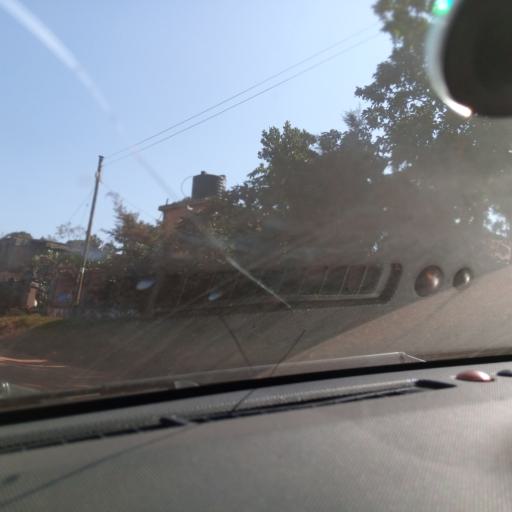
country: UG
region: Central Region
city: Masaka
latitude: -0.3389
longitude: 31.7321
